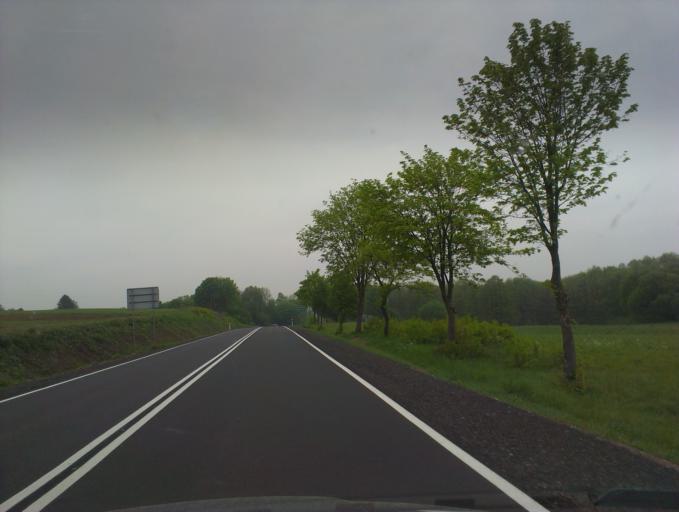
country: PL
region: West Pomeranian Voivodeship
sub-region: Powiat koszalinski
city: Bobolice
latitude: 53.9454
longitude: 16.5888
